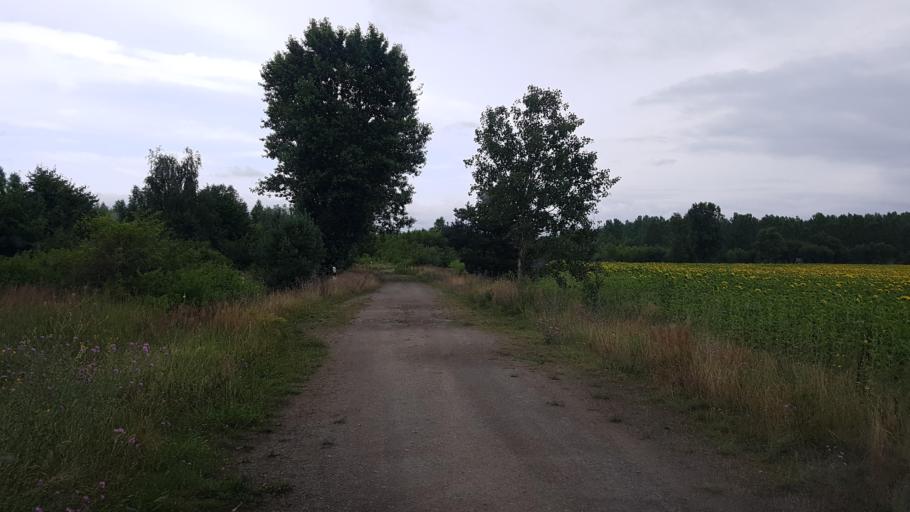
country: DE
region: Brandenburg
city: Spremberg
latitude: 51.5956
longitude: 14.3208
